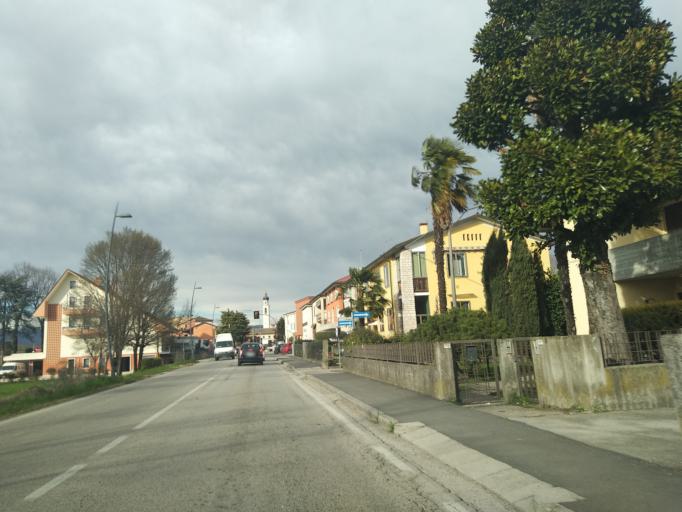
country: IT
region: Veneto
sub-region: Provincia di Vicenza
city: Bolzano Vicentino
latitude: 45.5997
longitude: 11.6218
